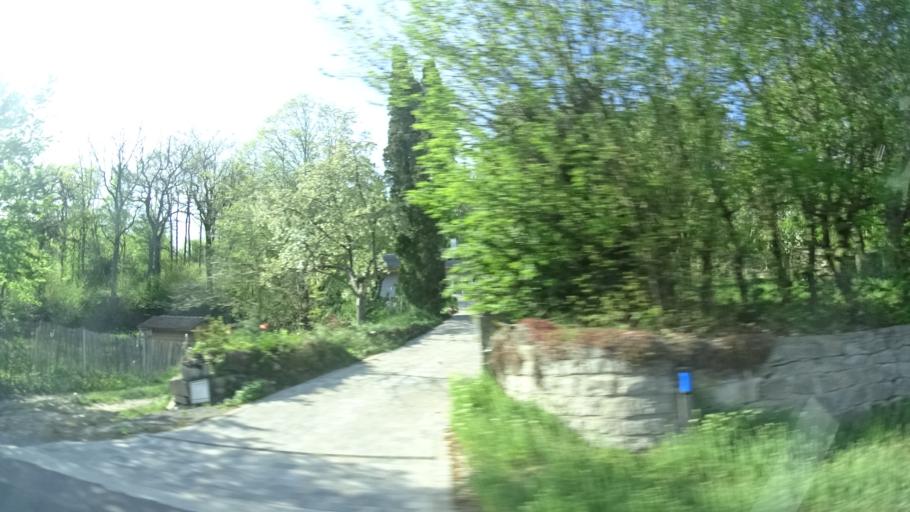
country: DE
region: Bavaria
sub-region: Regierungsbezirk Unterfranken
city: Wonfurt
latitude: 50.0237
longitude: 10.4681
